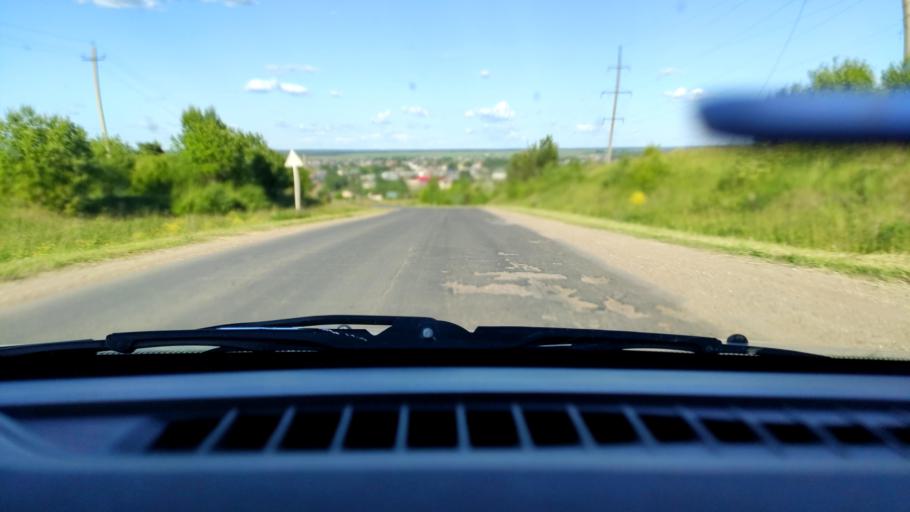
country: RU
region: Perm
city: Orda
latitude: 57.1887
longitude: 56.8827
